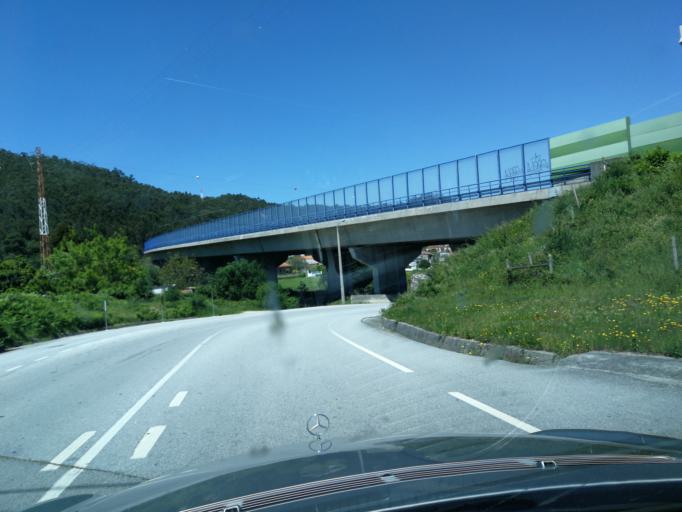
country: PT
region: Viana do Castelo
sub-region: Viana do Castelo
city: Meadela
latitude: 41.7187
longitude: -8.7983
